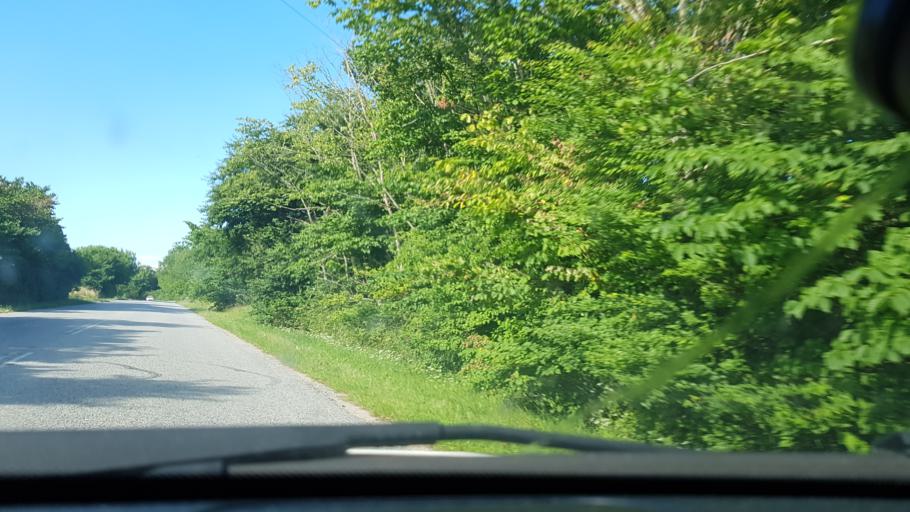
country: DK
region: Zealand
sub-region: Odsherred Kommune
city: Hojby
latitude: 55.8908
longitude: 11.6137
